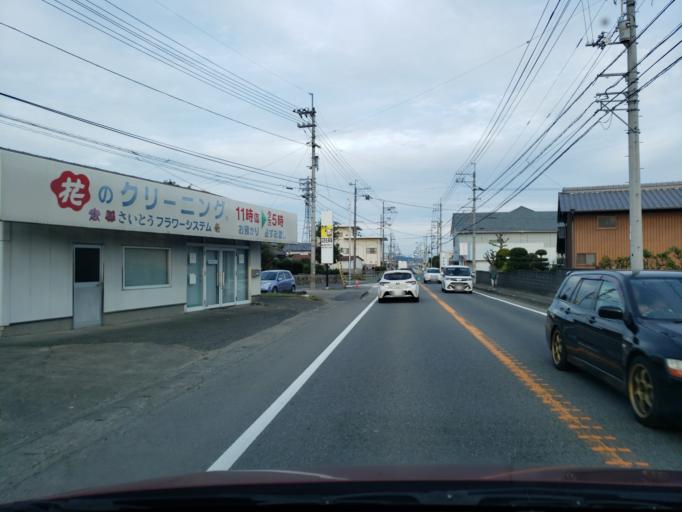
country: JP
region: Tokushima
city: Kamojimacho-jogejima
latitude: 34.0917
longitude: 134.3052
